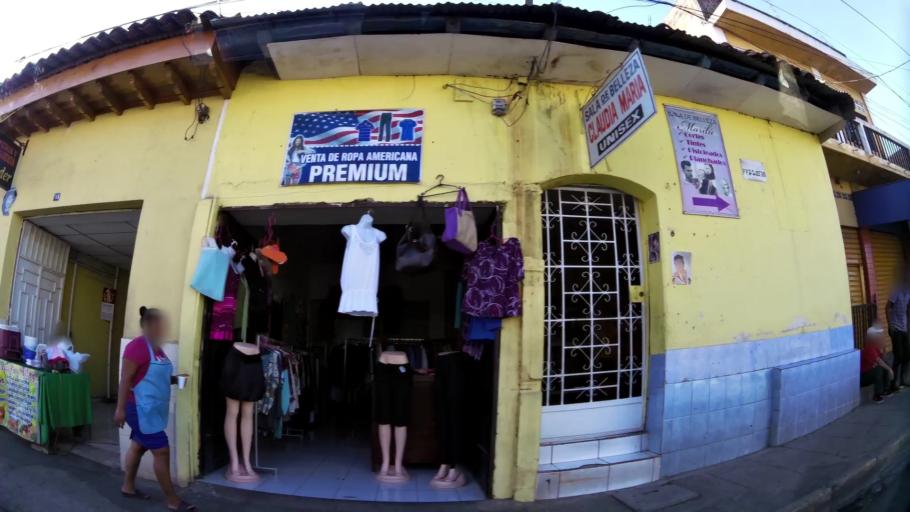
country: SV
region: San Miguel
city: San Miguel
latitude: 13.4796
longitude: -88.1766
